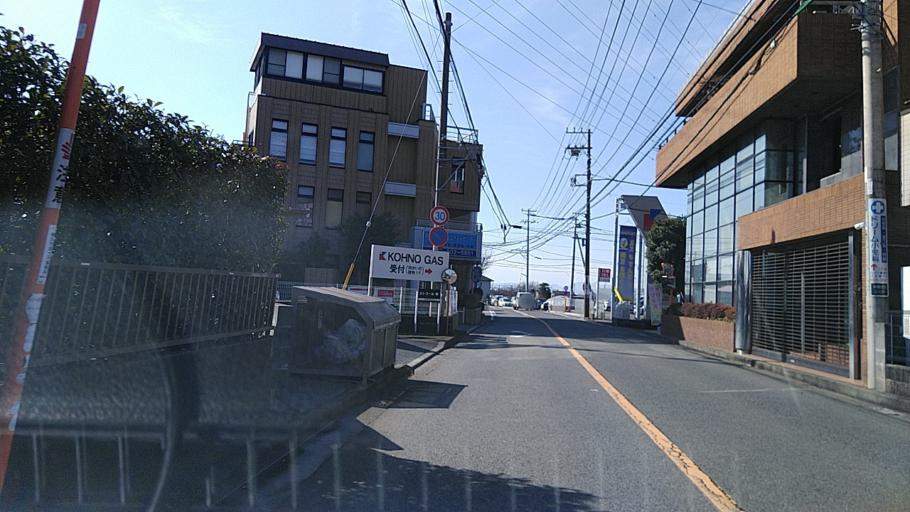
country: JP
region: Kanagawa
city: Fujisawa
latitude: 35.4044
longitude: 139.4963
